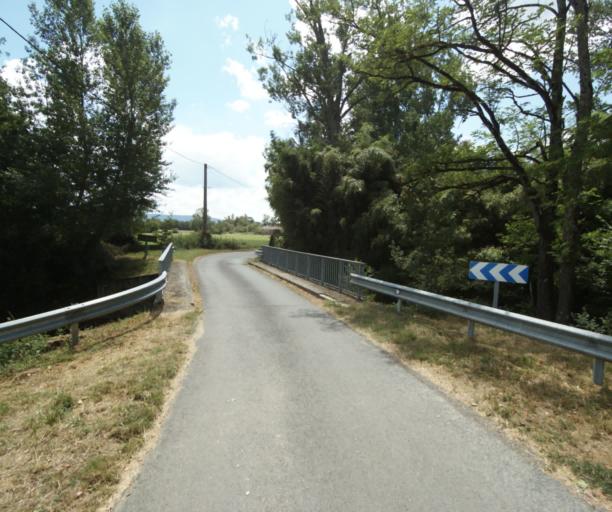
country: FR
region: Midi-Pyrenees
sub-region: Departement du Tarn
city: Puylaurens
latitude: 43.5203
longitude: 2.0225
